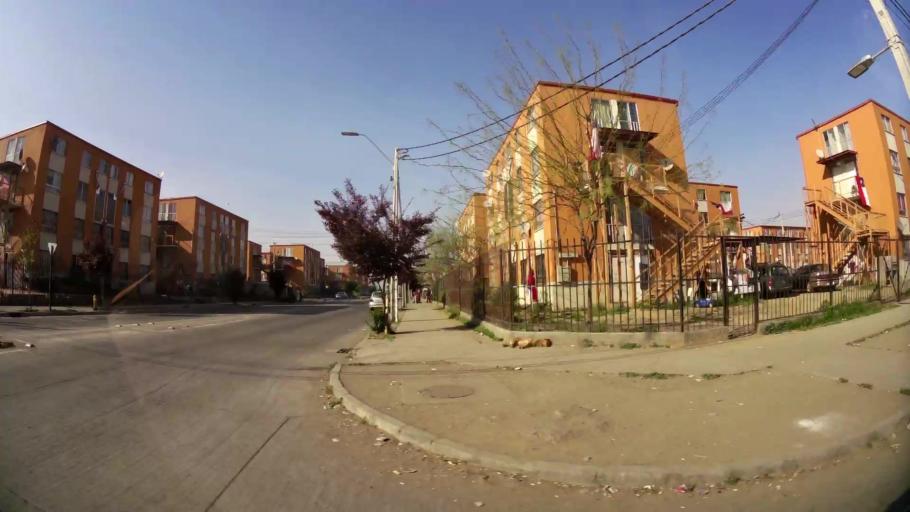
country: CL
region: Santiago Metropolitan
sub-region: Provincia de Santiago
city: Lo Prado
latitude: -33.4198
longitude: -70.7633
